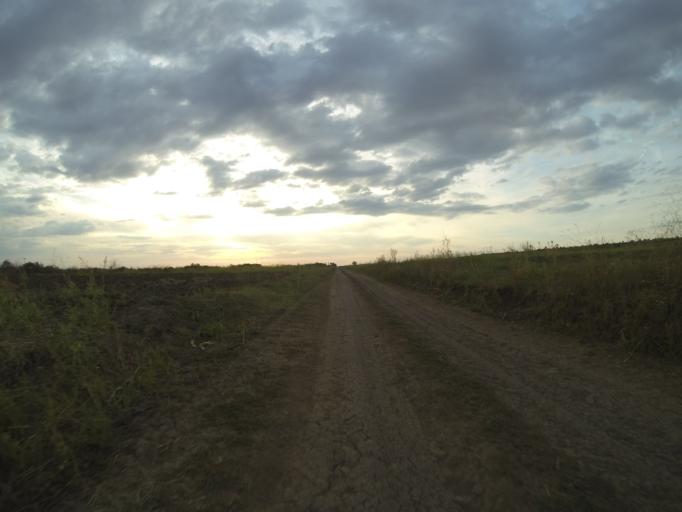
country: RO
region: Dolj
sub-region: Comuna Ceratu
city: Ceratu
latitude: 44.1008
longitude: 23.6746
